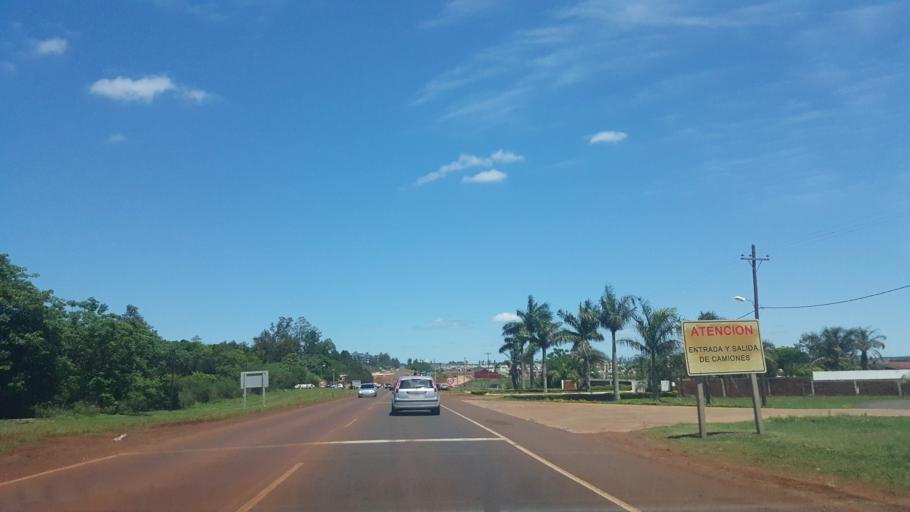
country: AR
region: Misiones
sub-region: Departamento de Capital
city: Posadas
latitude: -27.4079
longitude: -55.9752
